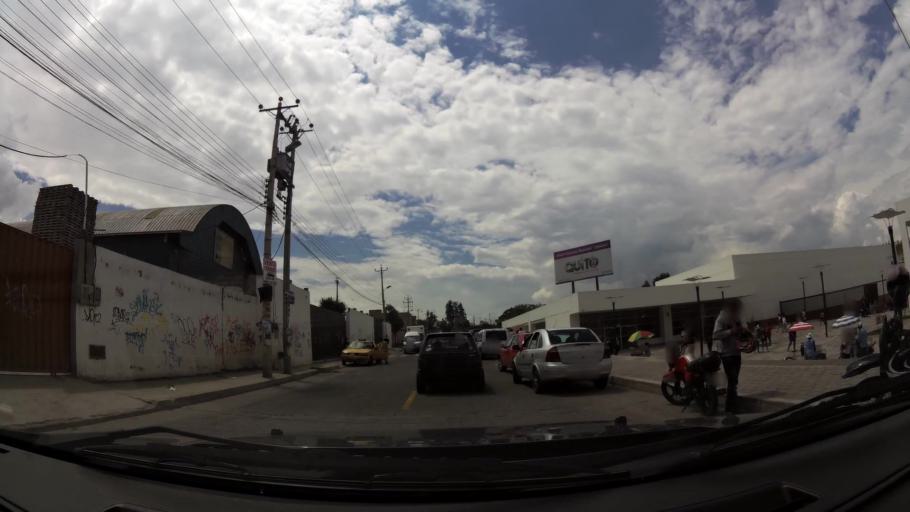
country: EC
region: Pichincha
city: Quito
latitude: -0.0759
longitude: -78.4168
